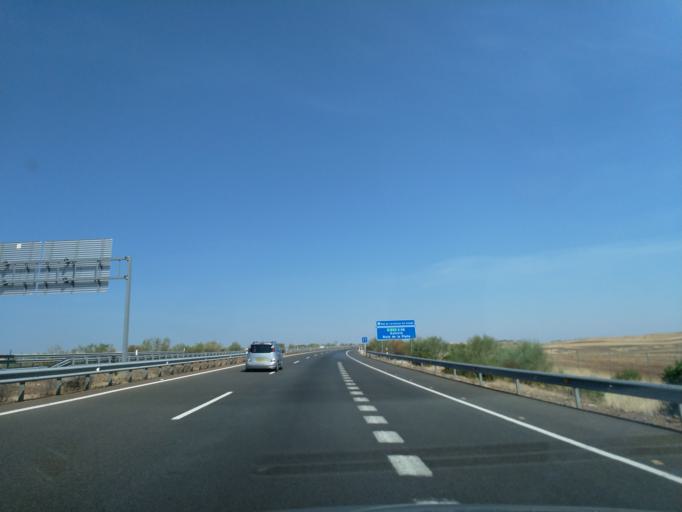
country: ES
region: Extremadura
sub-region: Provincia de Badajoz
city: Merida
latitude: 38.9551
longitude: -6.3437
